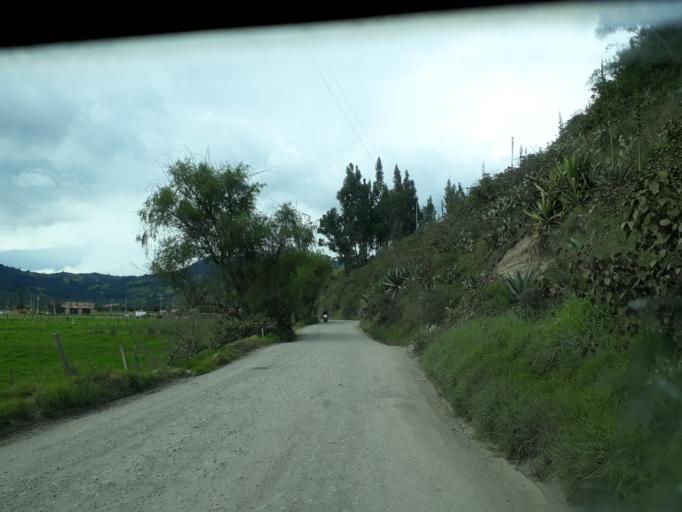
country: CO
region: Cundinamarca
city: Cucunuba
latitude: 5.2505
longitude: -73.7844
